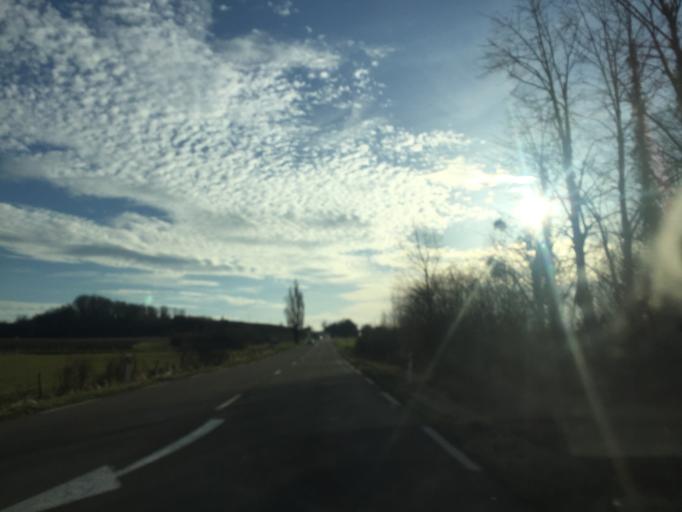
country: FR
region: Franche-Comte
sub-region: Departement du Jura
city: Arbois
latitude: 46.9379
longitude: 5.7777
